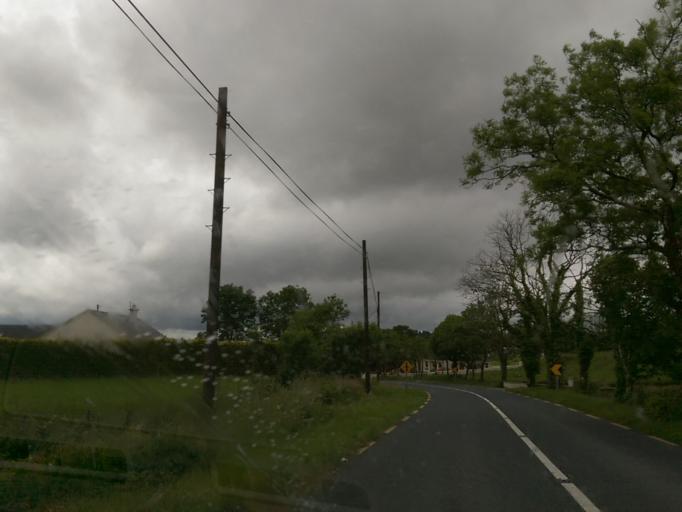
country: IE
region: Munster
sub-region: An Clar
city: Ennis
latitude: 52.7698
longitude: -9.0938
